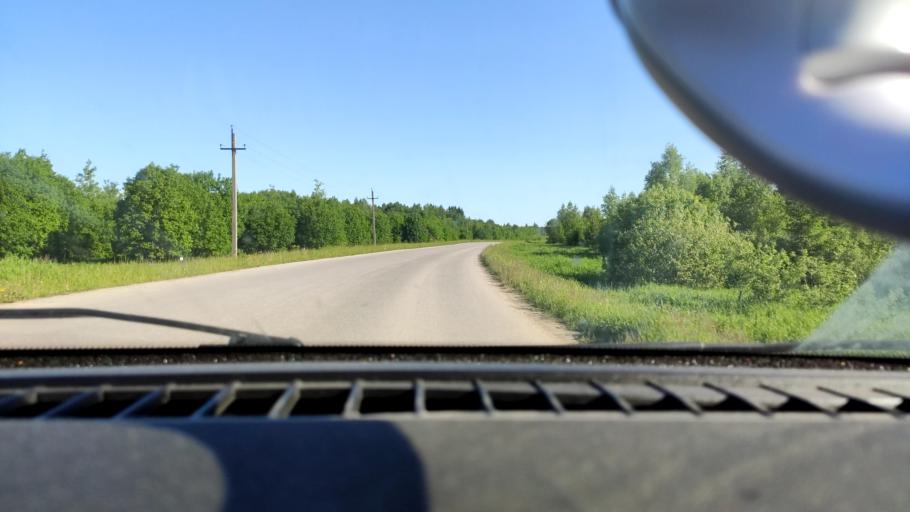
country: RU
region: Perm
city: Polazna
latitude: 58.2001
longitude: 56.5321
